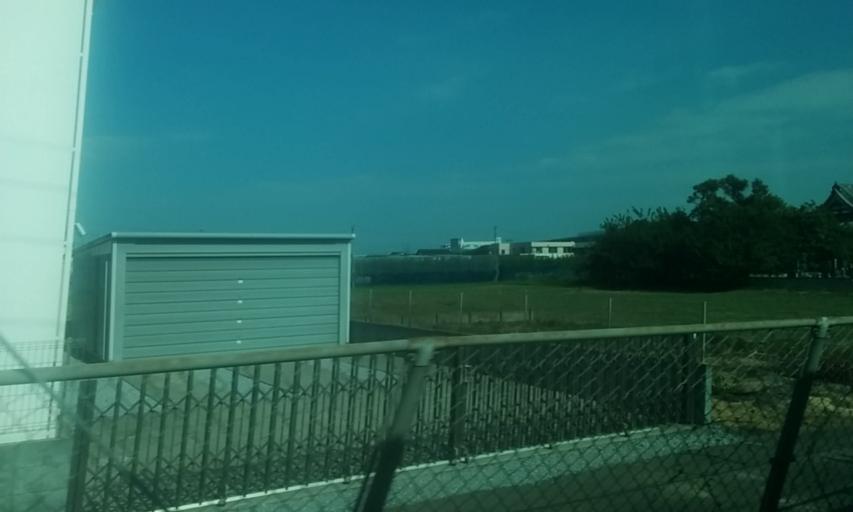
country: JP
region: Saitama
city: Kukichuo
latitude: 36.0417
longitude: 139.6725
